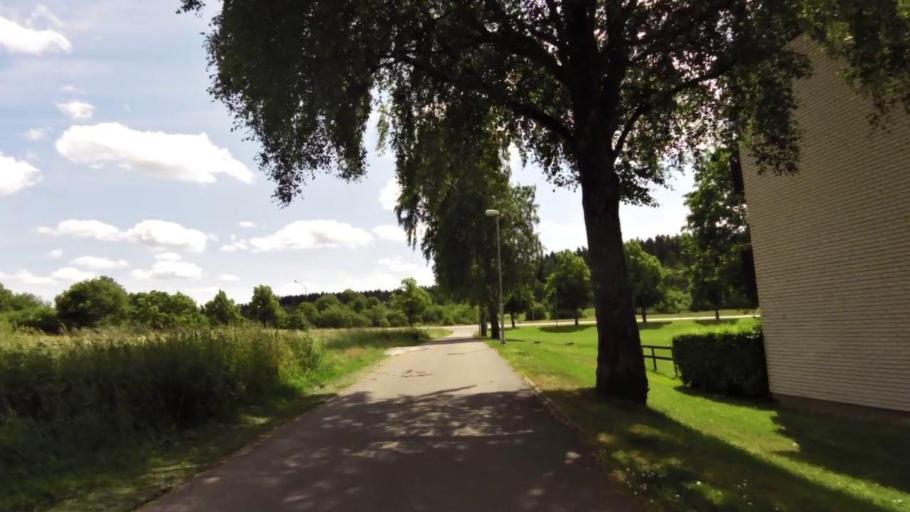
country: SE
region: OEstergoetland
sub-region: Linkopings Kommun
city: Linkoping
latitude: 58.4224
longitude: 15.5791
